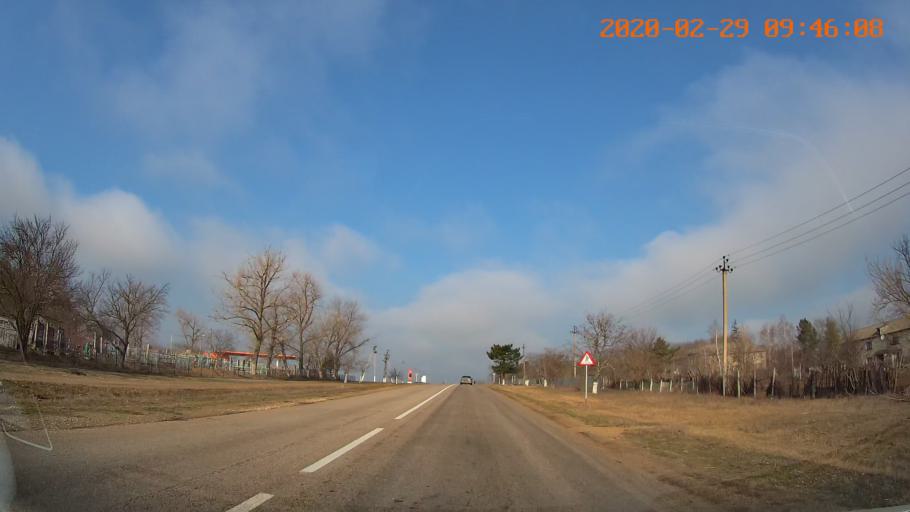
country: MD
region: Telenesti
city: Crasnoe
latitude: 46.6644
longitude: 29.8019
